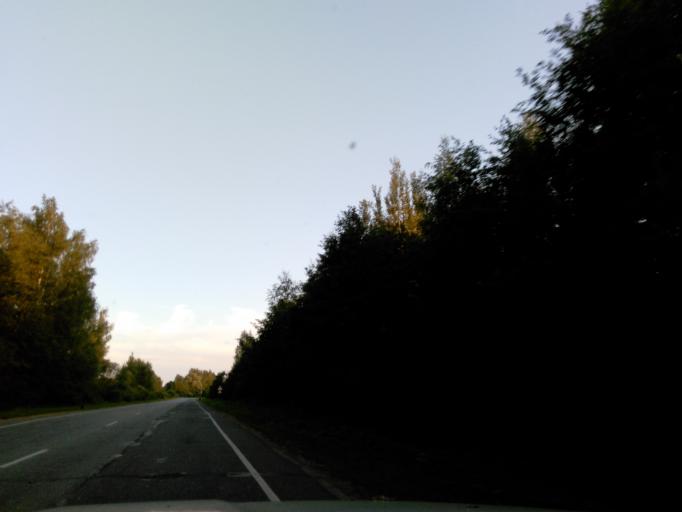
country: RU
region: Tverskaya
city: Konakovo
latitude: 56.6462
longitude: 36.7088
